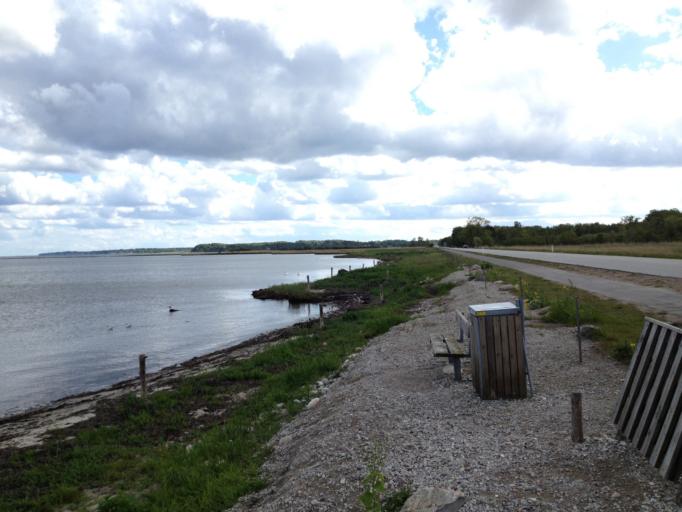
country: DK
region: Capital Region
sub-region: Fredensborg Kommune
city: Niva
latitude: 55.9348
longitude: 12.5225
